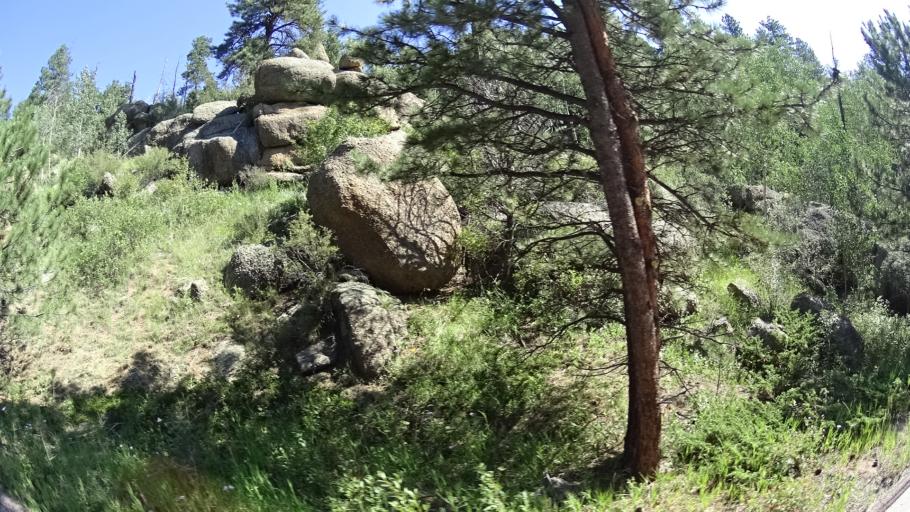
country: US
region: Colorado
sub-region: El Paso County
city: Cascade-Chipita Park
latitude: 38.9017
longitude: -105.0023
